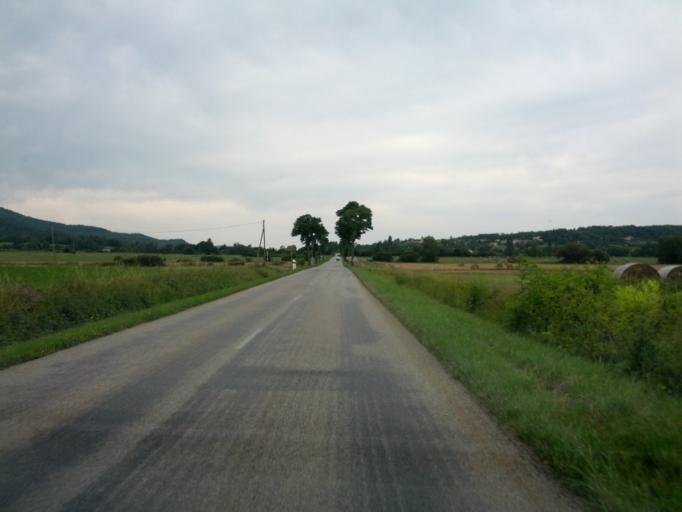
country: FR
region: Languedoc-Roussillon
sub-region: Departement de l'Aude
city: Quillan
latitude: 42.8870
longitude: 2.1288
